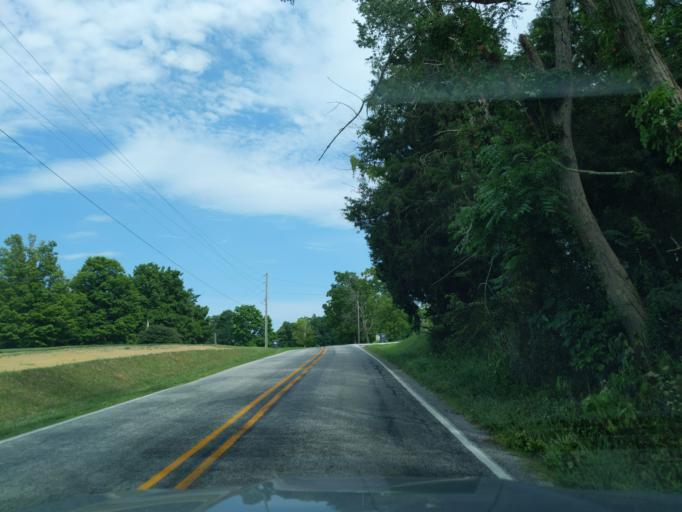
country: US
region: Indiana
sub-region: Ripley County
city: Osgood
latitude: 39.1924
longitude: -85.2210
